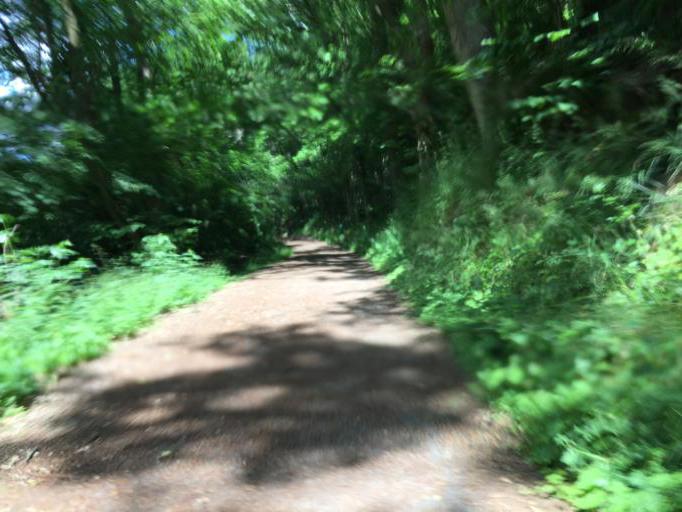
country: DE
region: Rheinland-Pfalz
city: Holler
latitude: 50.4306
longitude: 7.8468
